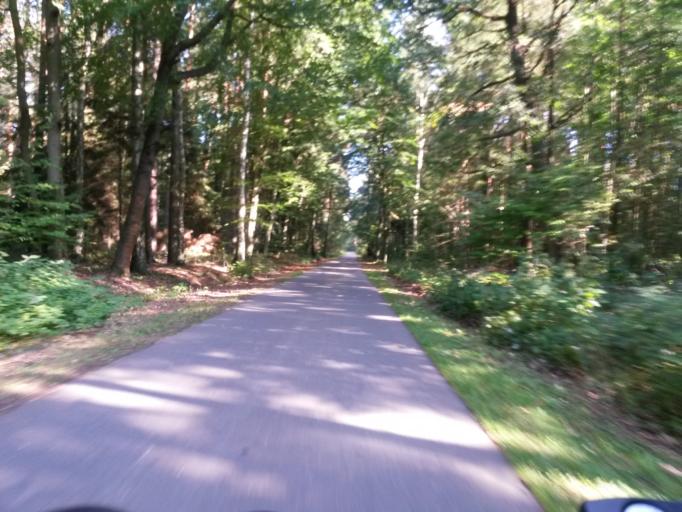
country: DE
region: Brandenburg
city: Templin
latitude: 53.1627
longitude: 13.4392
